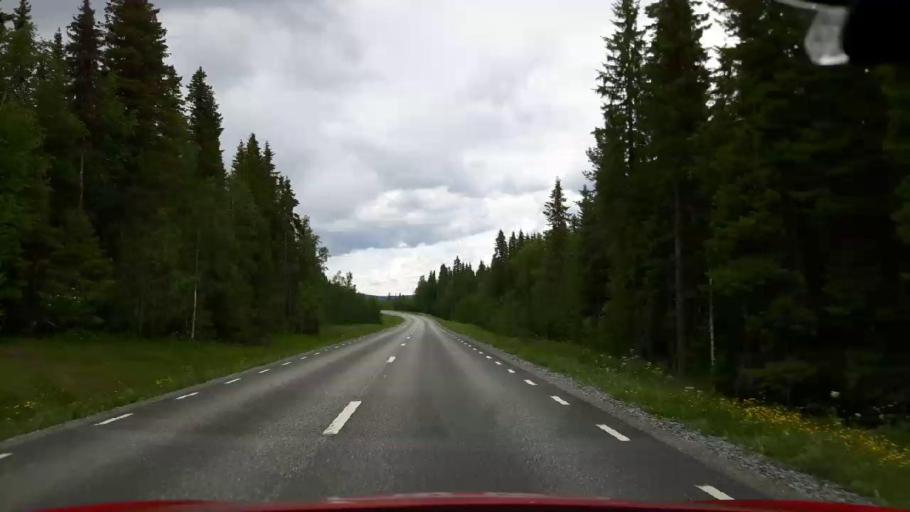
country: SE
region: Jaemtland
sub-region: Krokoms Kommun
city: Krokom
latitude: 63.6973
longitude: 14.3193
